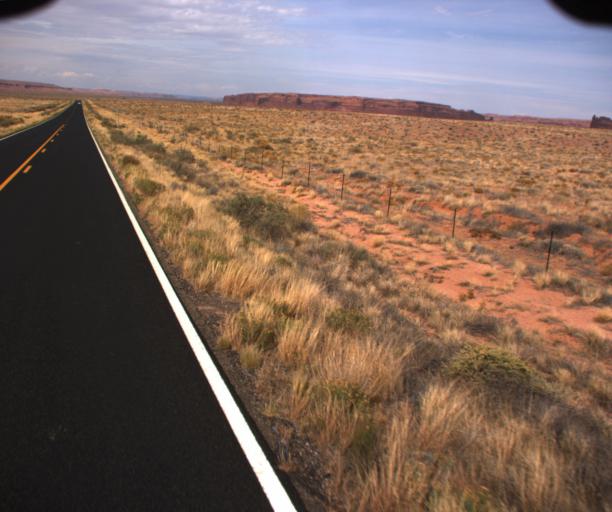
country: US
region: Arizona
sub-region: Apache County
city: Many Farms
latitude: 36.5539
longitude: -109.5337
